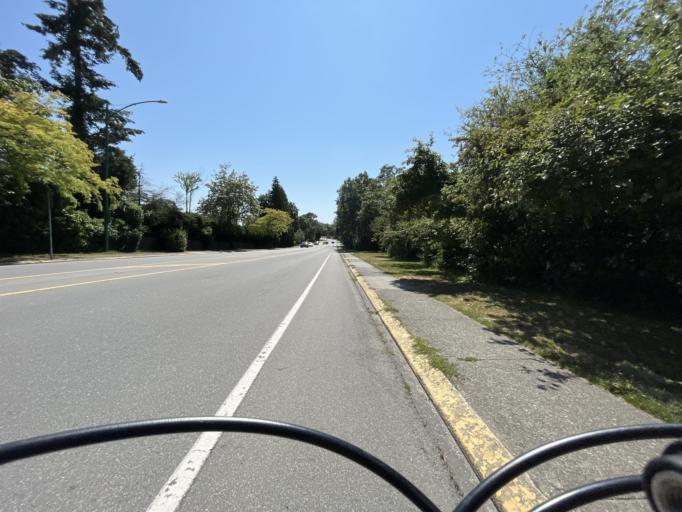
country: CA
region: British Columbia
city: Oak Bay
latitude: 48.4491
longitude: -123.3192
